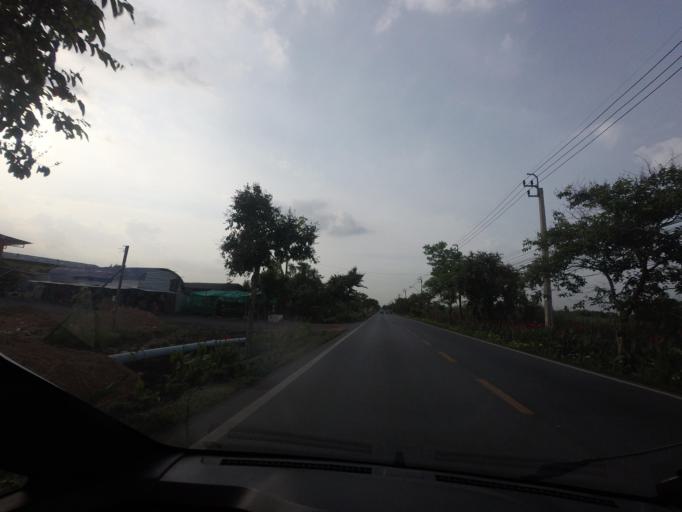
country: TH
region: Bangkok
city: Nong Chok
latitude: 13.8338
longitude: 100.8699
